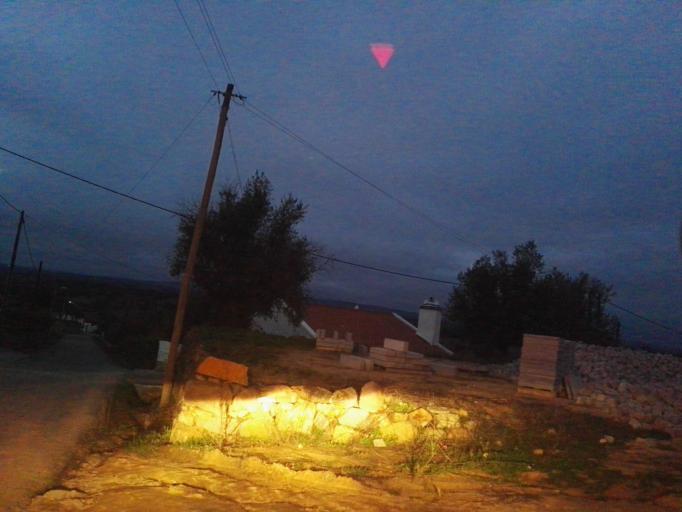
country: PT
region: Evora
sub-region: Viana do Alentejo
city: Viana do Alentejo
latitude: 38.3974
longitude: -8.1552
